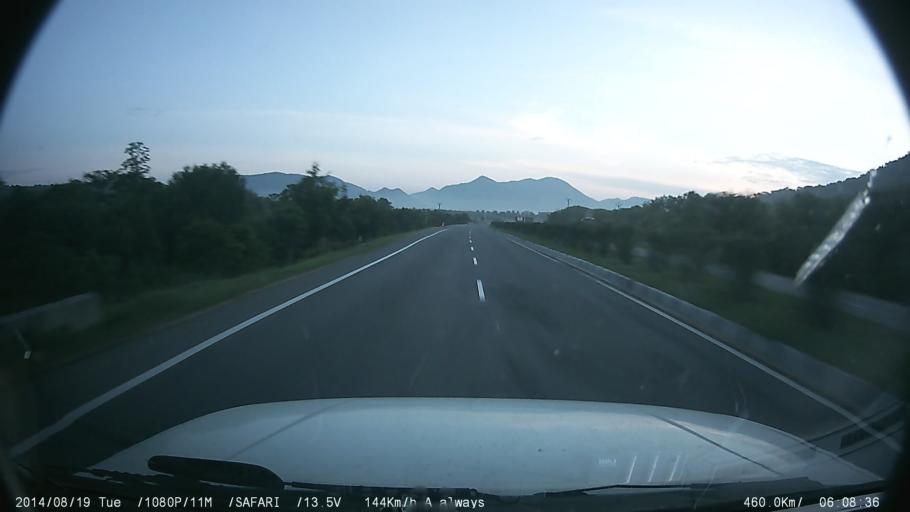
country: IN
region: Tamil Nadu
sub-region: Salem
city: Omalur
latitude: 11.9202
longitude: 78.0622
